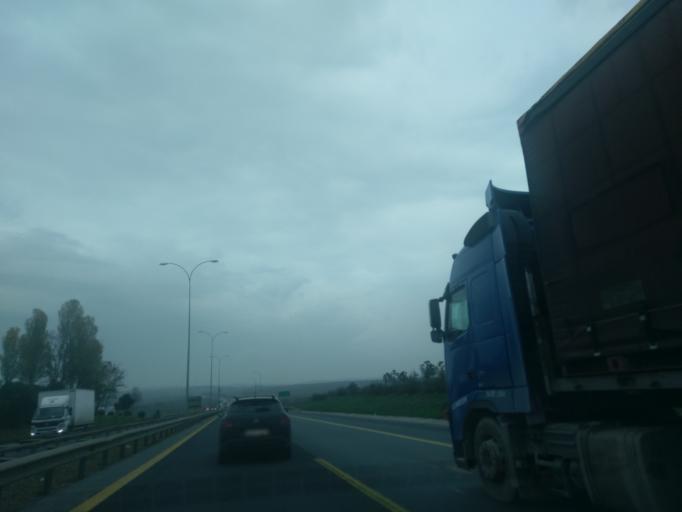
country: TR
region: Istanbul
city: Muratbey
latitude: 41.1063
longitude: 28.5535
